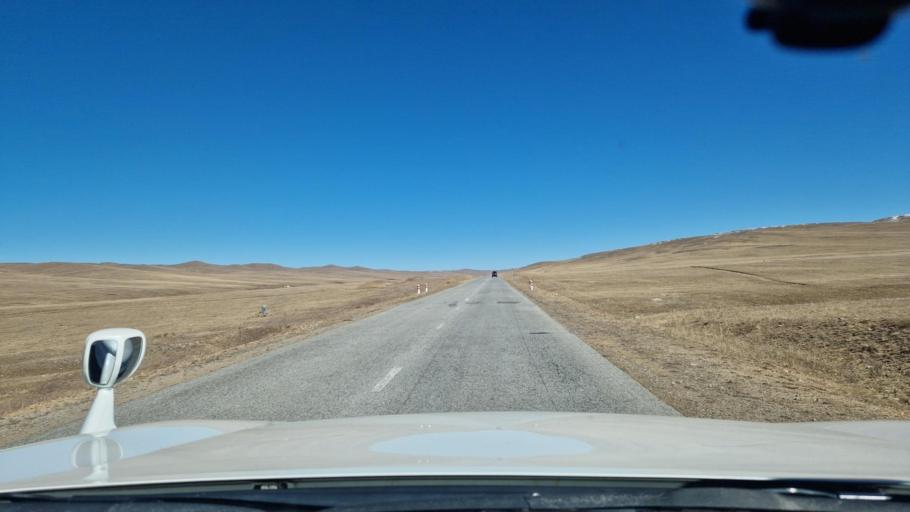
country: MN
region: Hentiy
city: Modot
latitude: 47.7397
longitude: 108.6048
